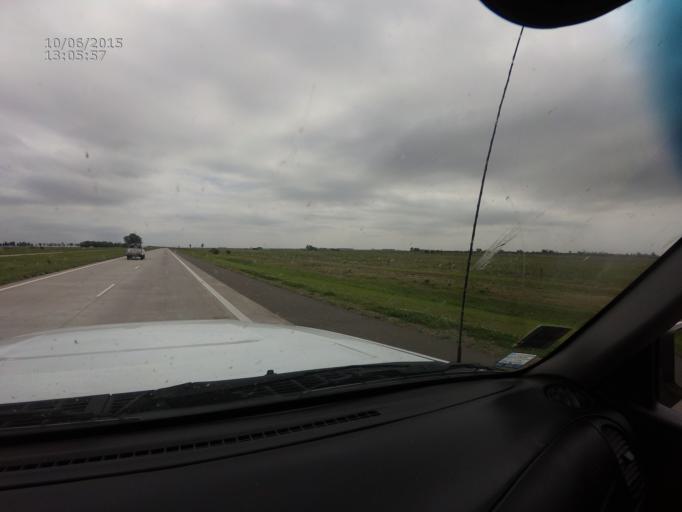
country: AR
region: Cordoba
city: General Roca
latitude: -32.7730
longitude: -61.8171
